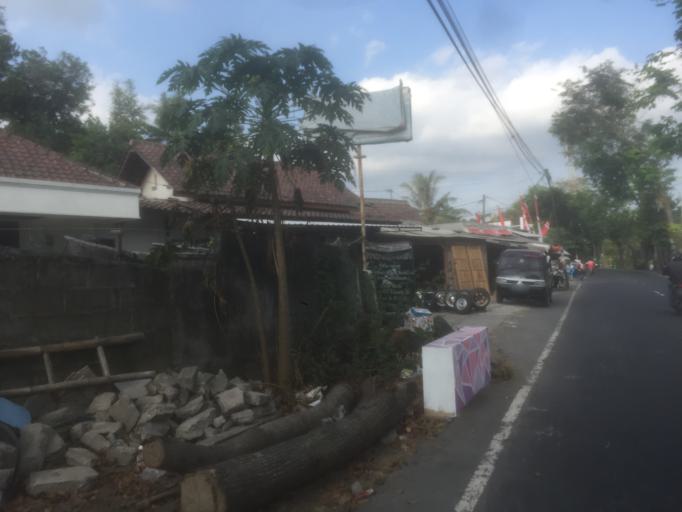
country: ID
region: Daerah Istimewa Yogyakarta
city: Melati
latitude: -7.7206
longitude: 110.3789
